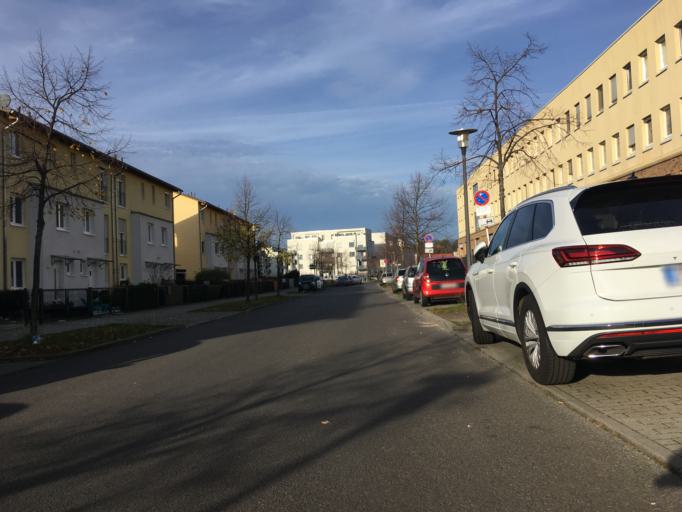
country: DE
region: Berlin
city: Biesdorf
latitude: 52.5045
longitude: 13.5573
